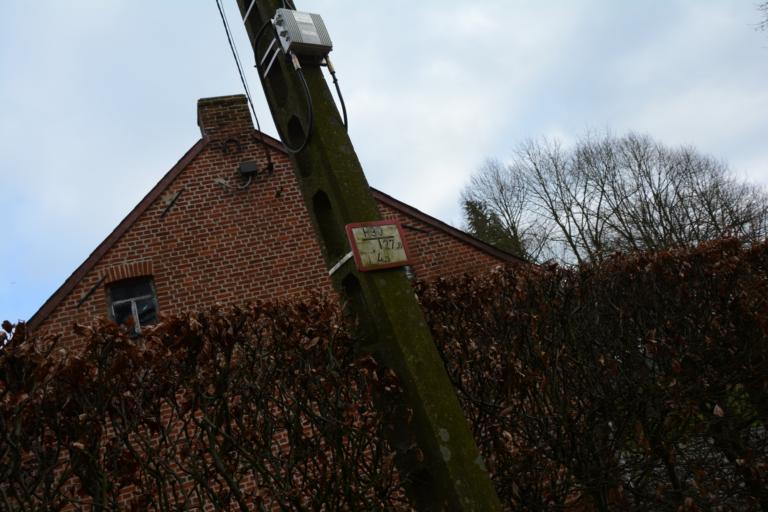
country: BE
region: Flanders
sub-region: Provincie Antwerpen
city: Herselt
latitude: 51.0483
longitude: 4.9143
